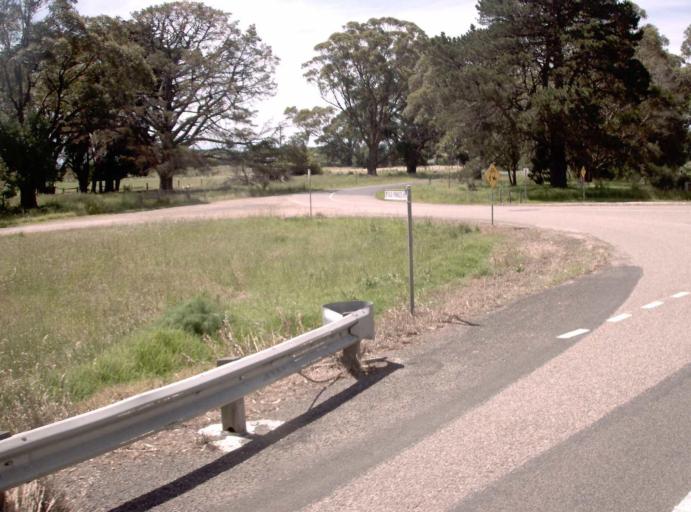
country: AU
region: Victoria
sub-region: Wellington
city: Sale
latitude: -37.9762
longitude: 147.0735
